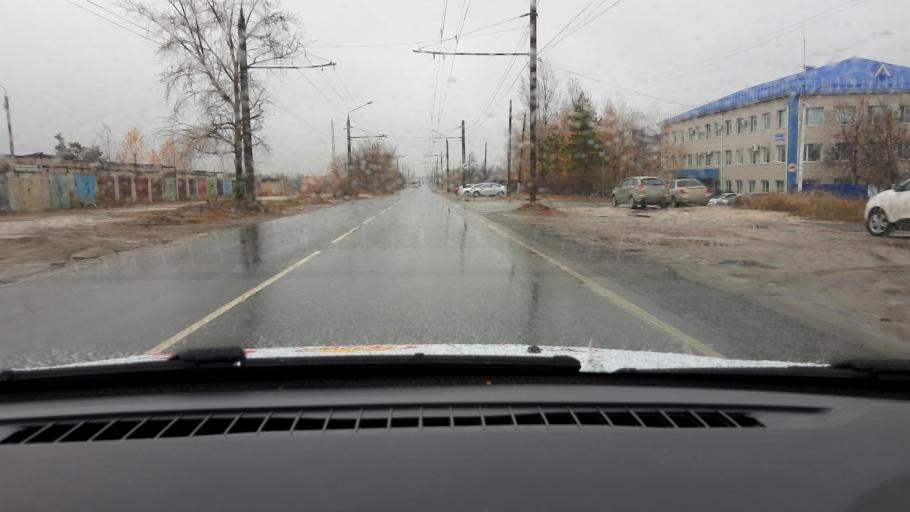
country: RU
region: Nizjnij Novgorod
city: Dzerzhinsk
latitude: 56.2490
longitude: 43.4895
